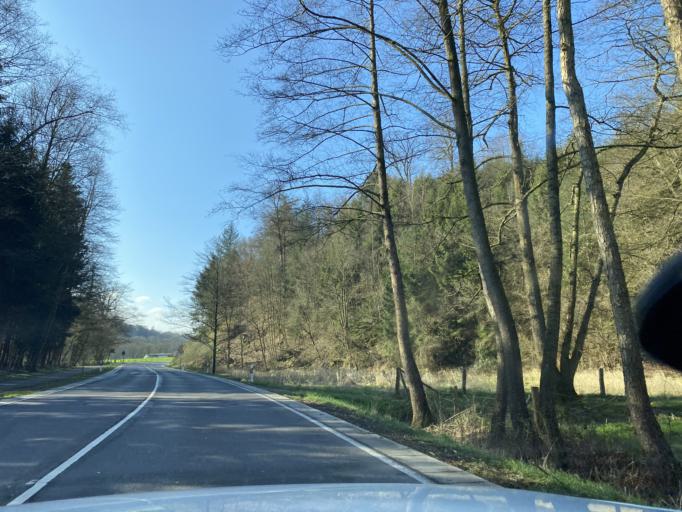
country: DE
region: North Rhine-Westphalia
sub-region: Regierungsbezirk Koln
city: Odenthal
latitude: 51.0452
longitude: 7.1235
